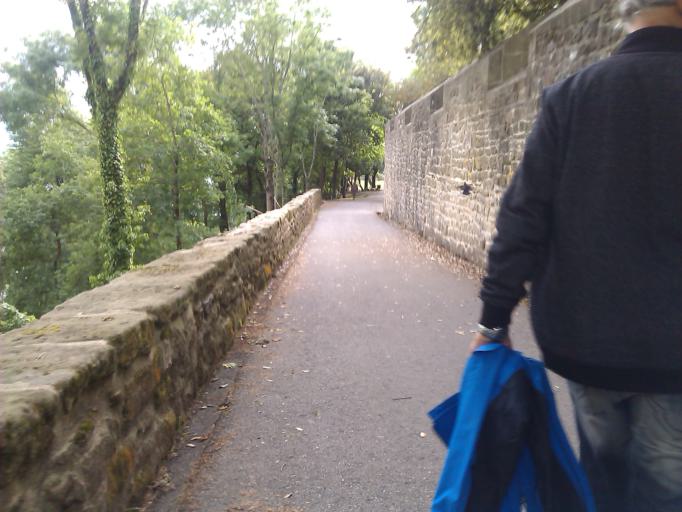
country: ES
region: Basque Country
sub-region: Provincia de Guipuzcoa
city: San Sebastian
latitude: 43.3245
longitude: -1.9895
